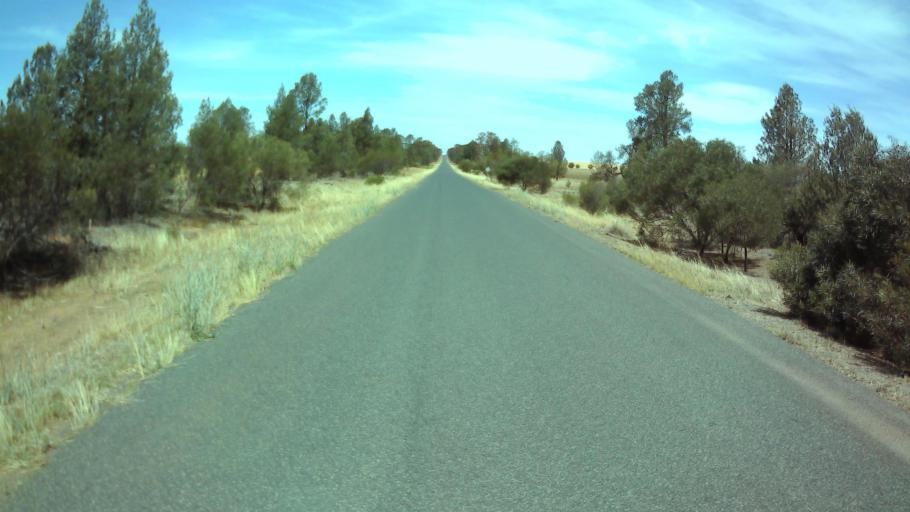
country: AU
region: New South Wales
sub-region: Weddin
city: Grenfell
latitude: -33.8911
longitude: 147.7440
